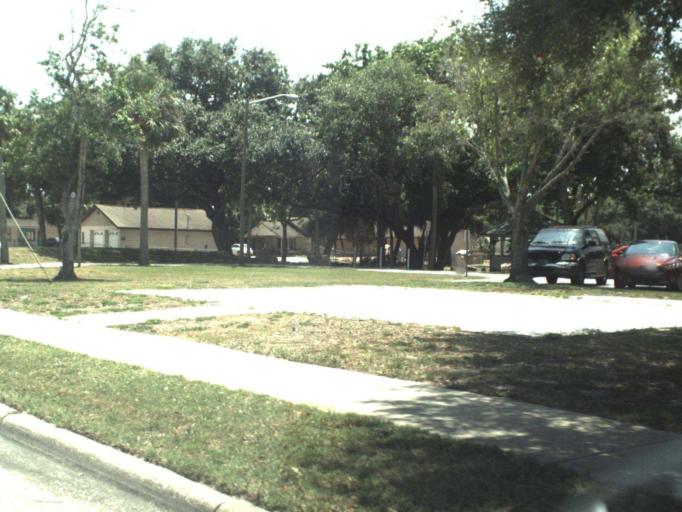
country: US
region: Florida
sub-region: Volusia County
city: Holly Hill
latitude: 29.2444
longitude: -81.0410
